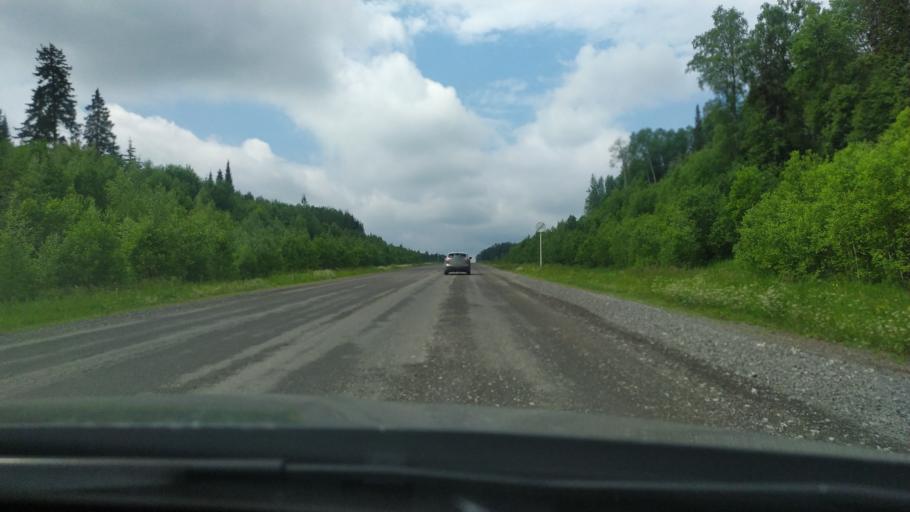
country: RU
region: Perm
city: Kalino
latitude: 58.2742
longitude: 57.3867
